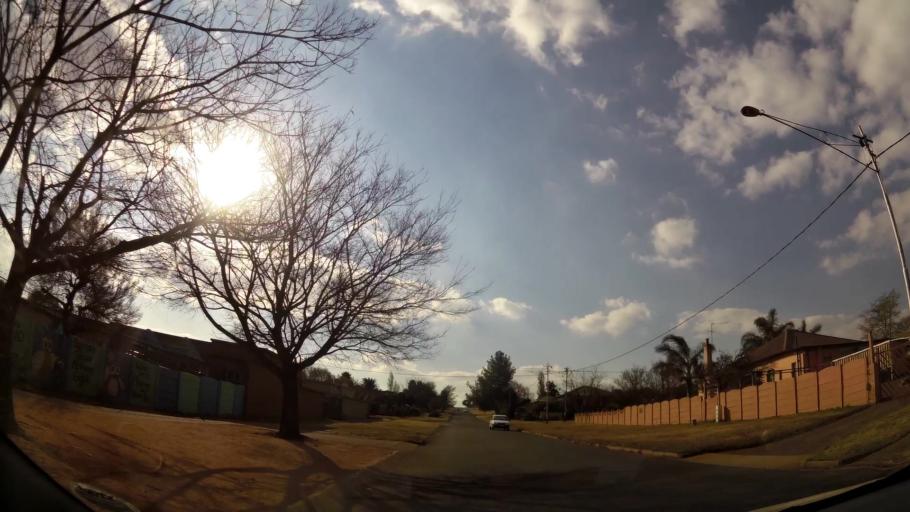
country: ZA
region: Gauteng
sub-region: West Rand District Municipality
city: Krugersdorp
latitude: -26.0874
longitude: 27.7654
